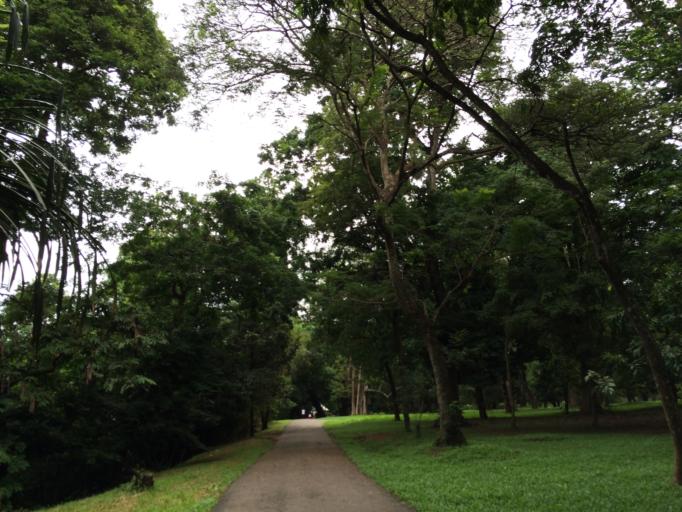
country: LK
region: Central
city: Kandy
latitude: 7.2736
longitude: 80.5932
